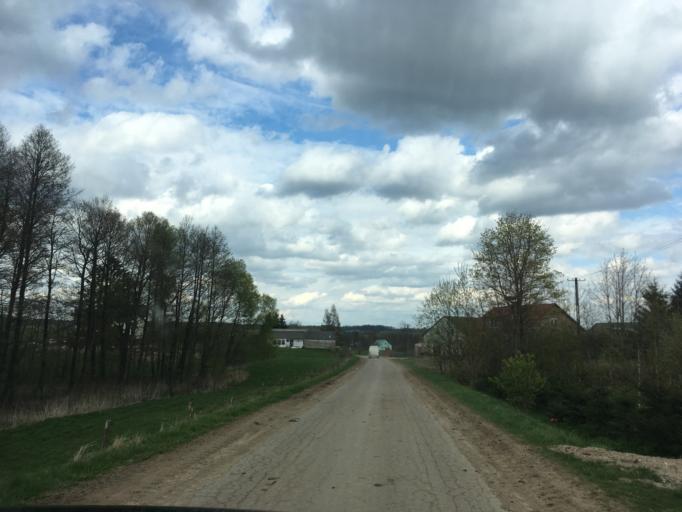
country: PL
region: Podlasie
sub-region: Suwalki
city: Suwalki
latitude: 54.3758
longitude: 22.9454
